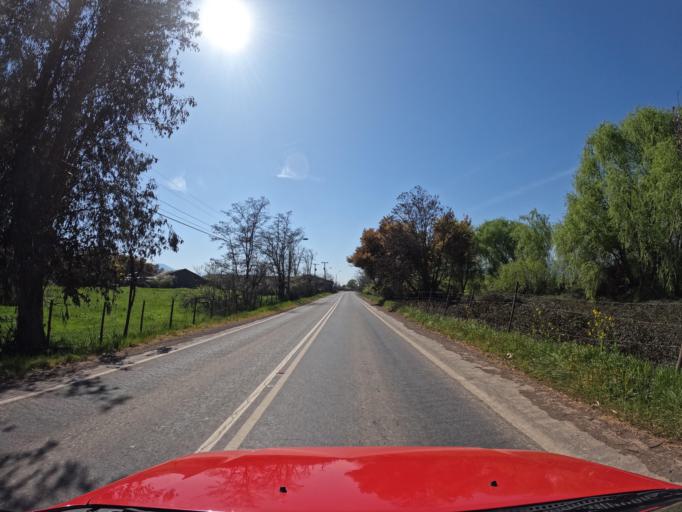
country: CL
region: Maule
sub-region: Provincia de Curico
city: Rauco
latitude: -35.0476
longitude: -71.4664
